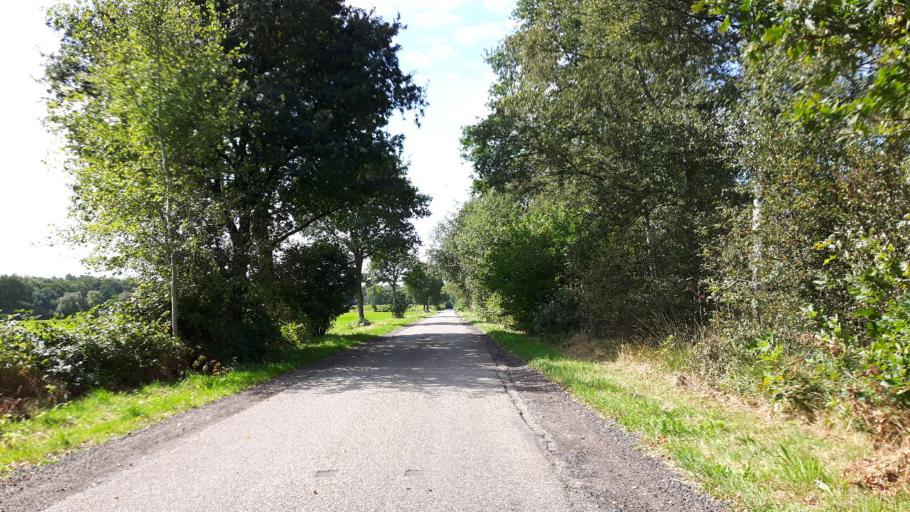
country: NL
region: Groningen
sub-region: Gemeente Leek
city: Leek
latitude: 53.0868
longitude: 6.3046
